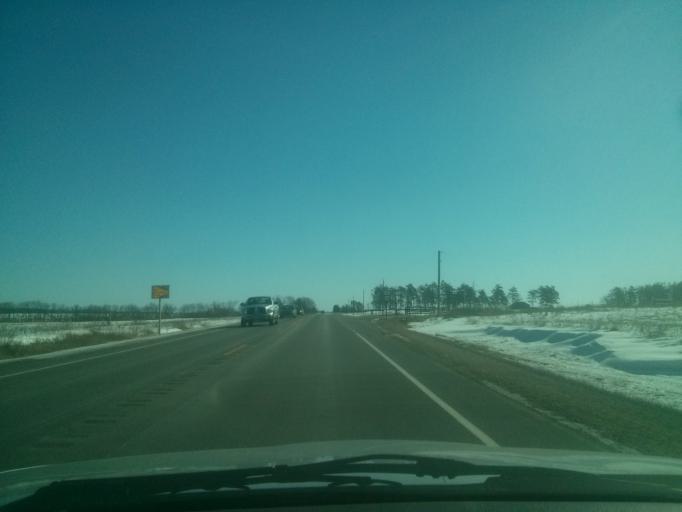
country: US
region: Wisconsin
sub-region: Polk County
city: Clear Lake
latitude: 45.1364
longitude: -92.3544
